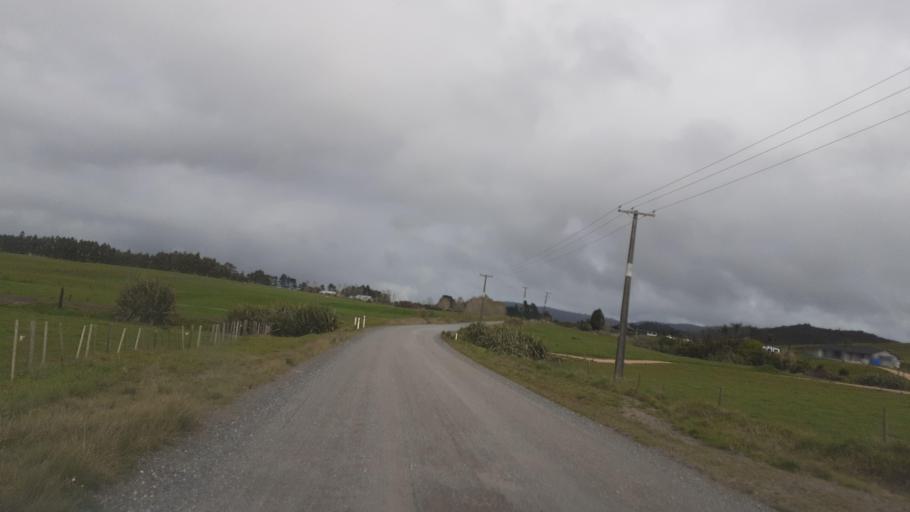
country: NZ
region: Northland
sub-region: Far North District
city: Waimate North
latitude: -35.2437
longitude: 173.8041
